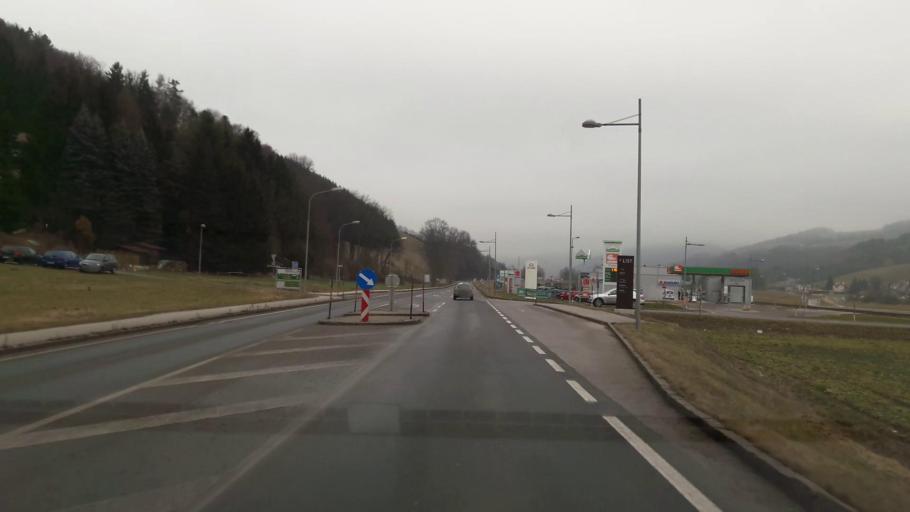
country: AT
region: Lower Austria
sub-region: Politischer Bezirk Neunkirchen
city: Grimmenstein
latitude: 47.6014
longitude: 16.1175
